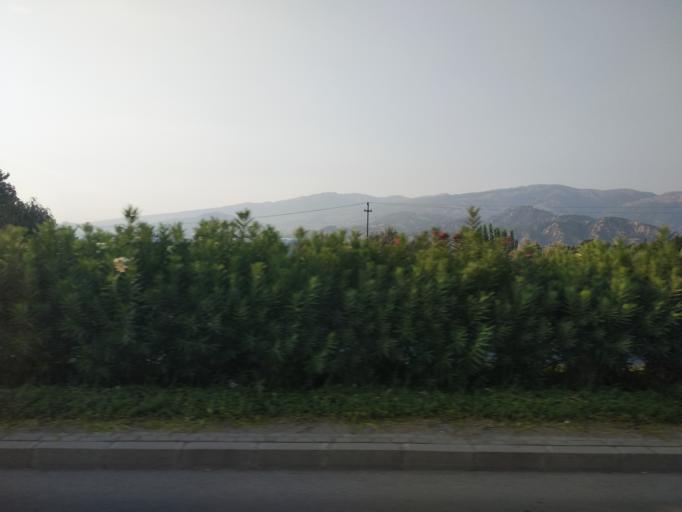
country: TR
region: Manisa
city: Salihli
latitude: 38.4938
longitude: 28.1763
